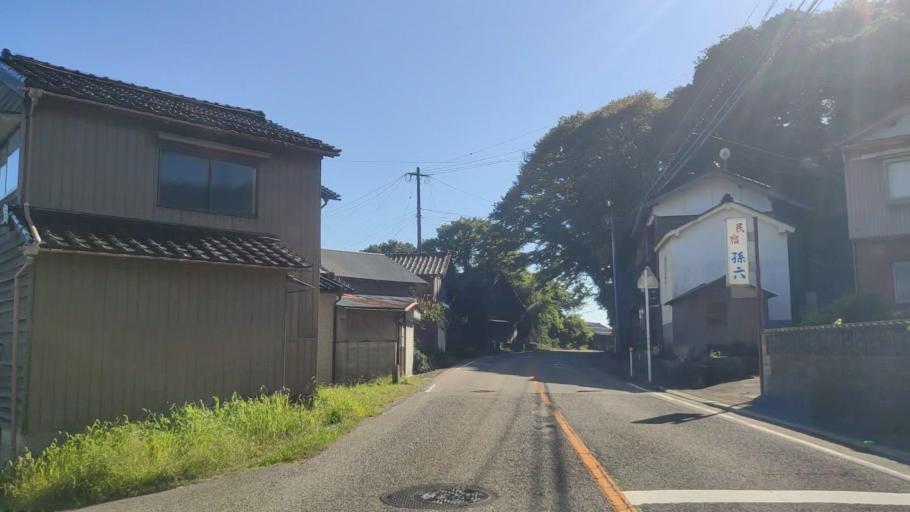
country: JP
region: Ishikawa
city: Nanao
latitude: 37.2950
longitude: 137.1365
